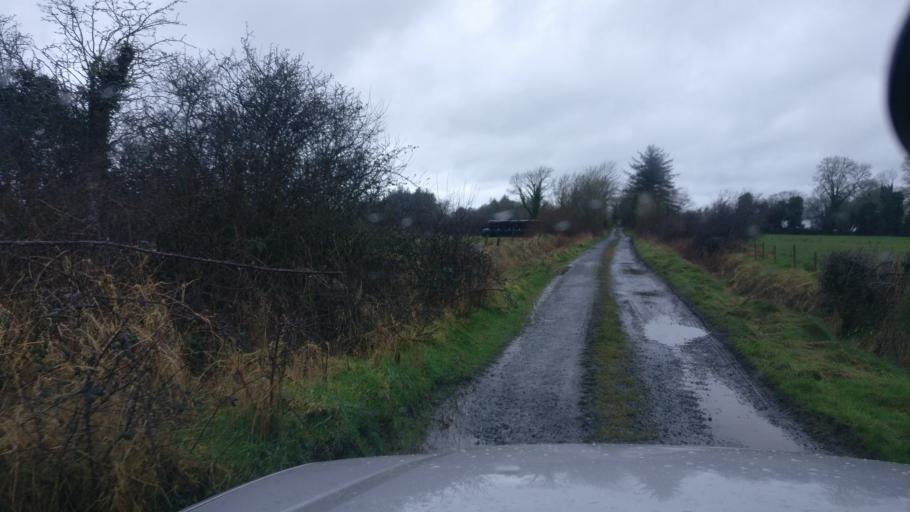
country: IE
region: Connaught
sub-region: County Galway
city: Ballinasloe
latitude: 53.2511
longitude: -8.3308
